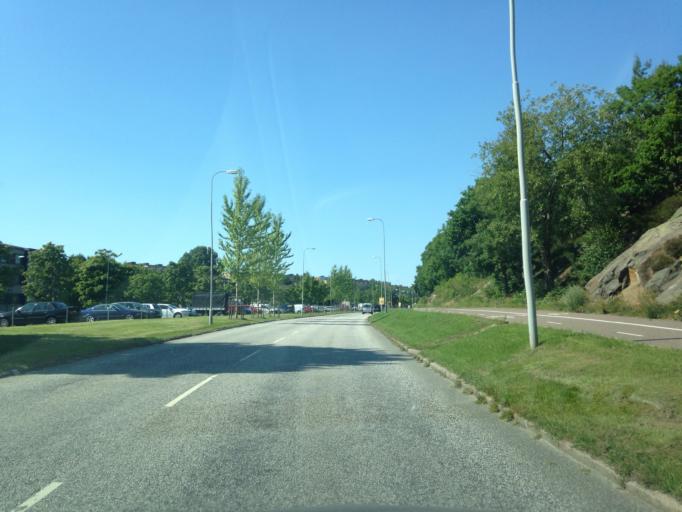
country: SE
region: Vaestra Goetaland
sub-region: Goteborg
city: Majorna
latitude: 57.7217
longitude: 11.9033
